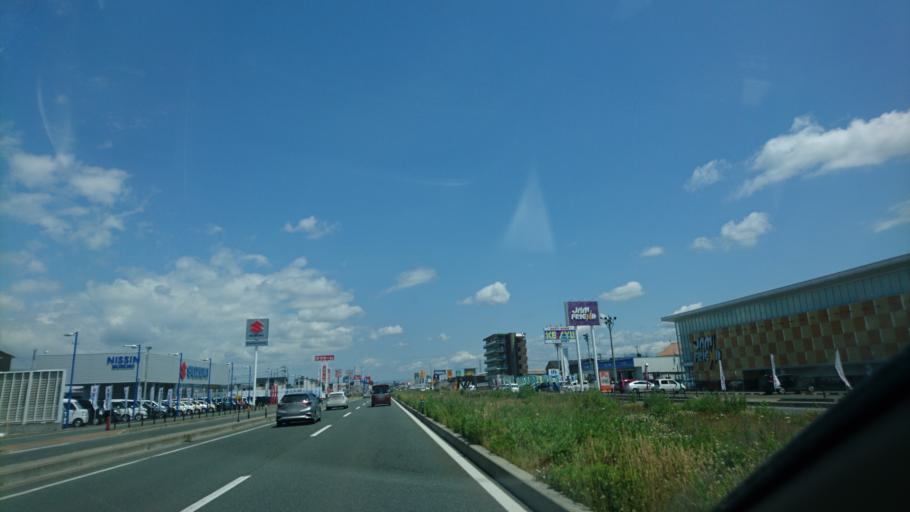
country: JP
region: Iwate
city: Morioka-shi
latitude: 39.6708
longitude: 141.1349
